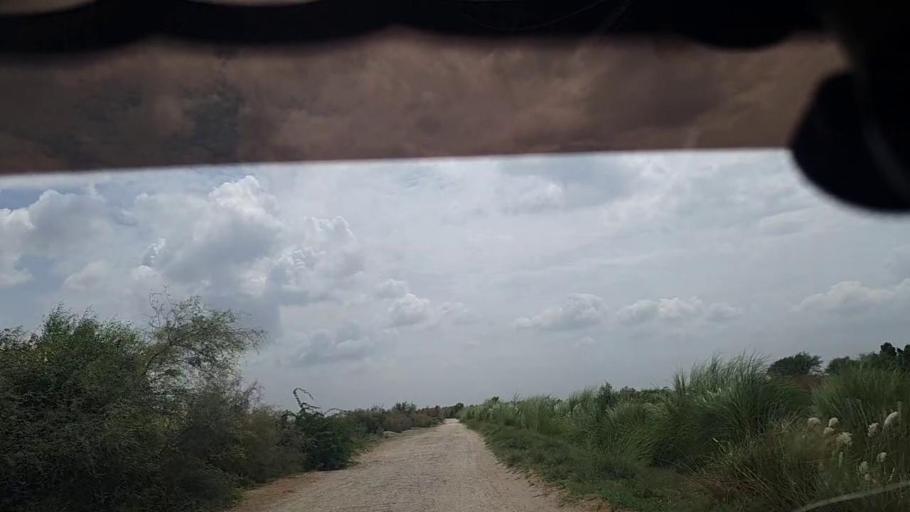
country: PK
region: Sindh
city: Rustam jo Goth
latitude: 28.0522
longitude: 68.9393
